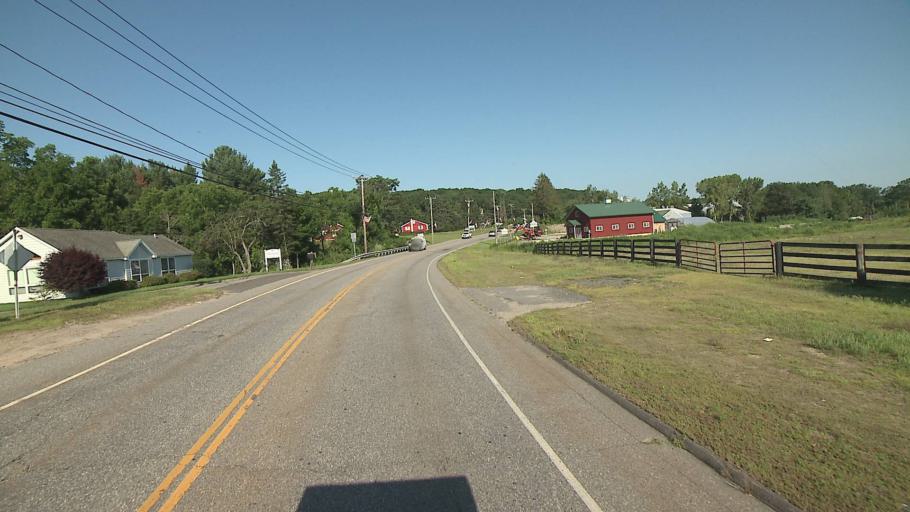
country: US
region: Connecticut
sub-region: Hartford County
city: Collinsville
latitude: 41.7691
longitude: -72.9674
